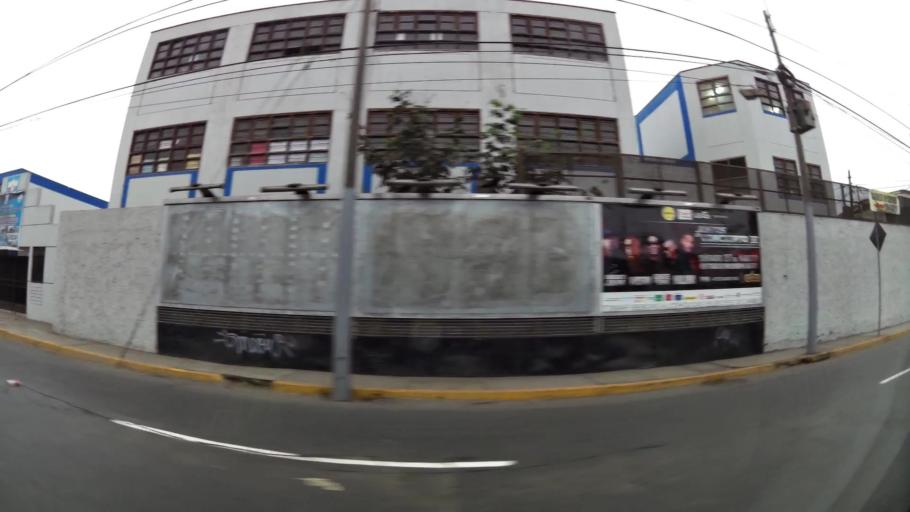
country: PE
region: Callao
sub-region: Callao
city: Callao
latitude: -12.0873
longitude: -77.0894
